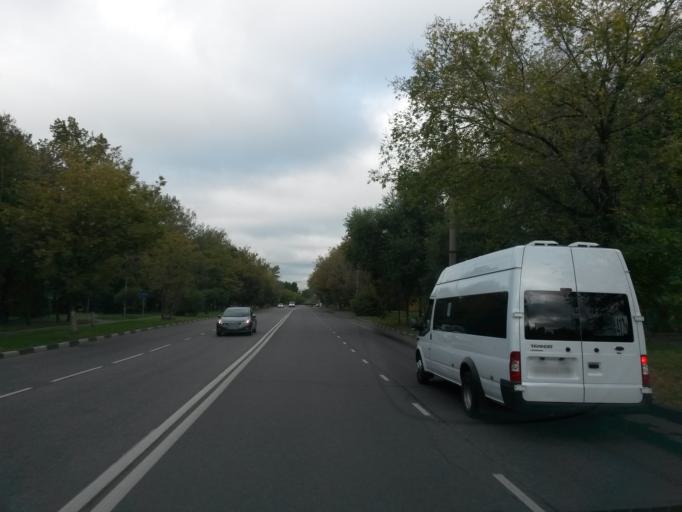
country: RU
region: Moscow
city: Kapotnya
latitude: 55.6423
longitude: 37.7930
